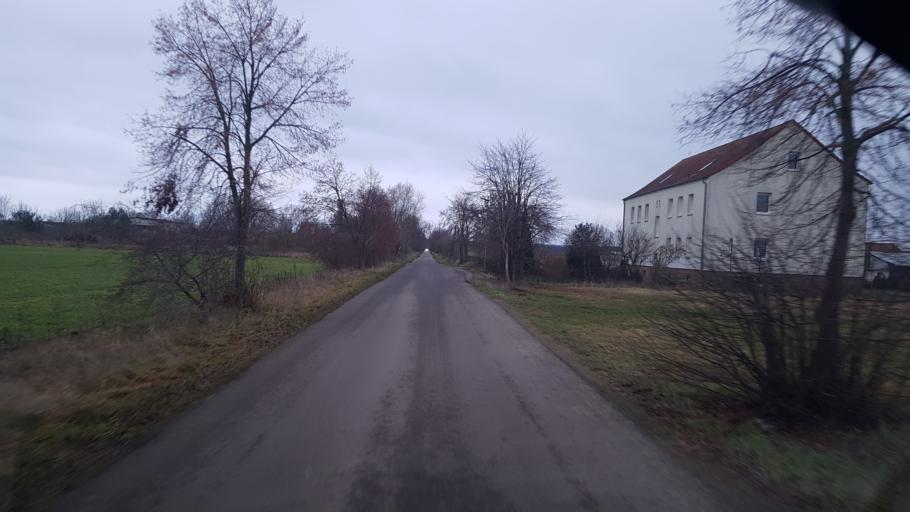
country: DE
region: Brandenburg
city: Ziltendorf
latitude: 52.2263
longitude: 14.6360
